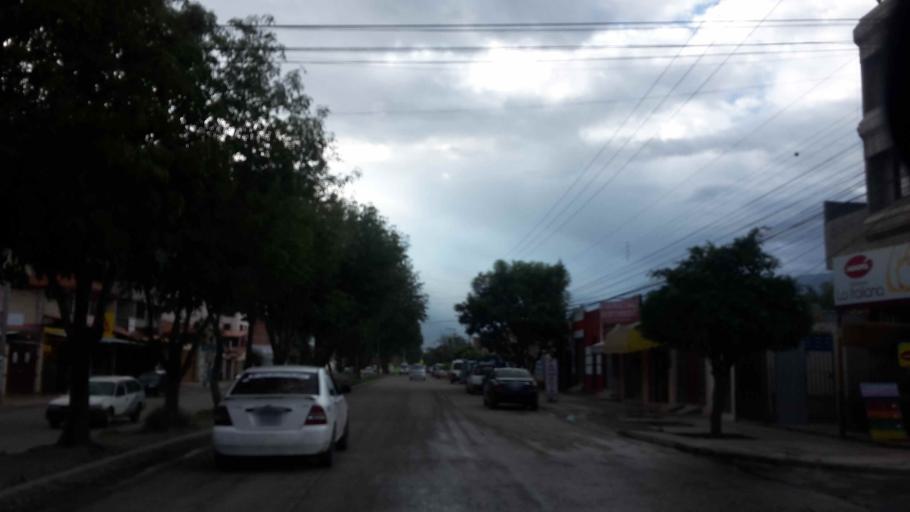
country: BO
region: Cochabamba
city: Cochabamba
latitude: -17.3591
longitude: -66.1719
